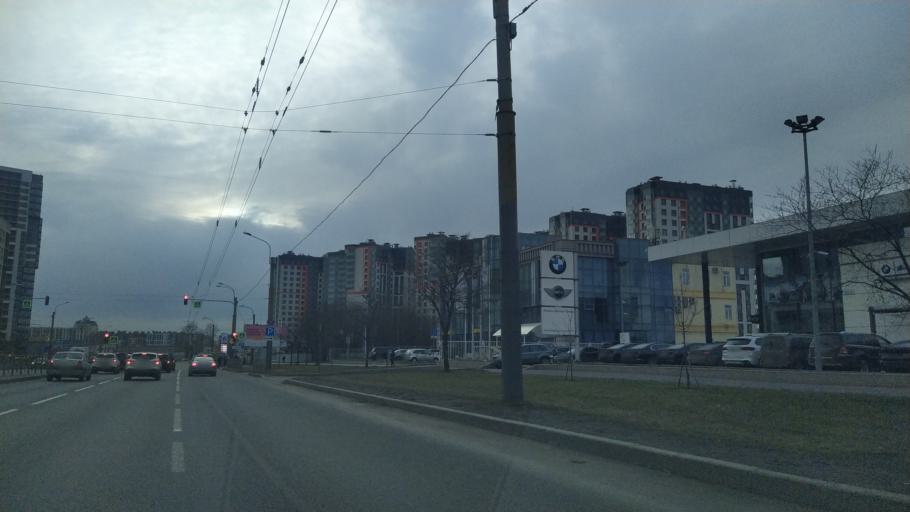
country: RU
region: St.-Petersburg
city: Kushelevka
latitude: 59.9895
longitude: 30.3721
